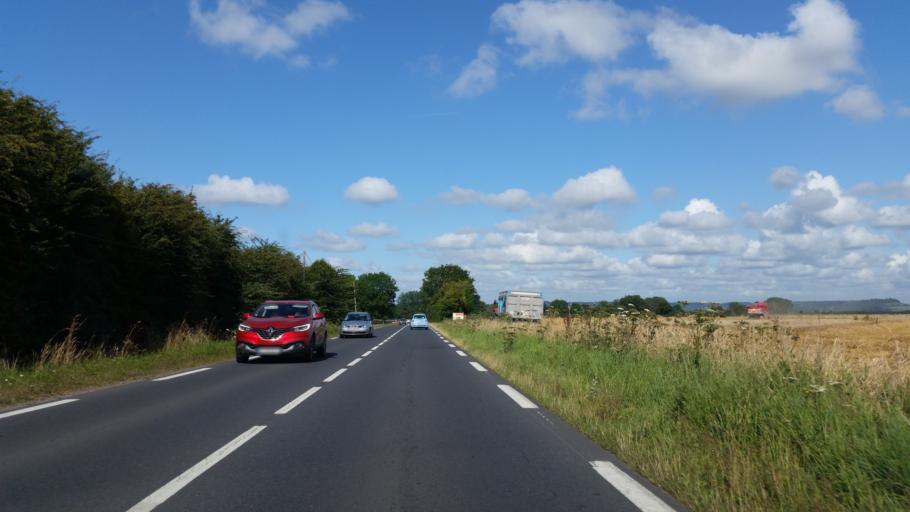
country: FR
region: Lower Normandy
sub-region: Departement du Calvados
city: Bavent
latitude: 49.2462
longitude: -0.1813
